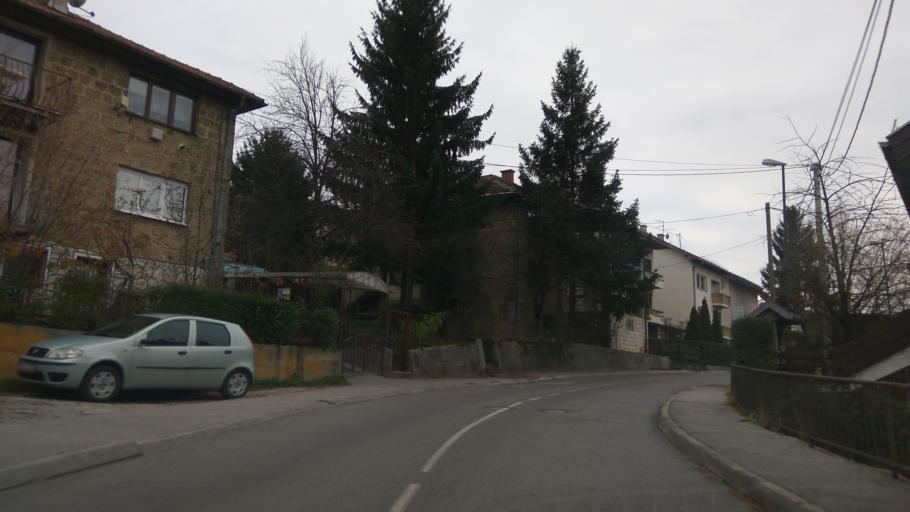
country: BA
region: Federation of Bosnia and Herzegovina
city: Kobilja Glava
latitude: 43.8620
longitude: 18.4037
